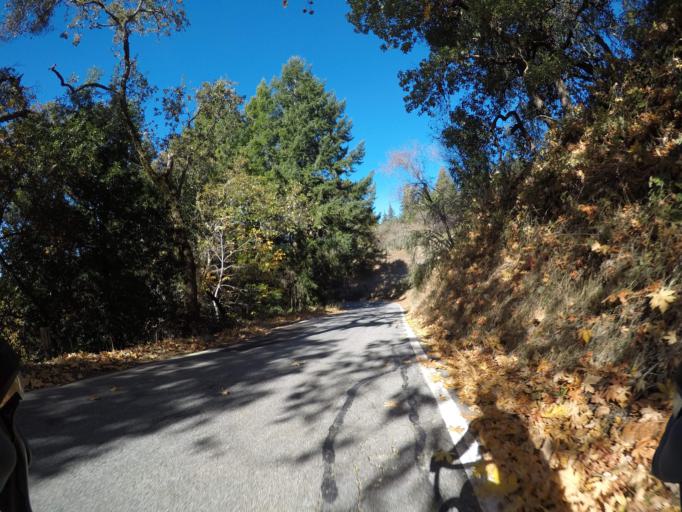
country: US
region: California
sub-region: Santa Clara County
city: Lexington Hills
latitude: 37.1589
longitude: -122.0065
